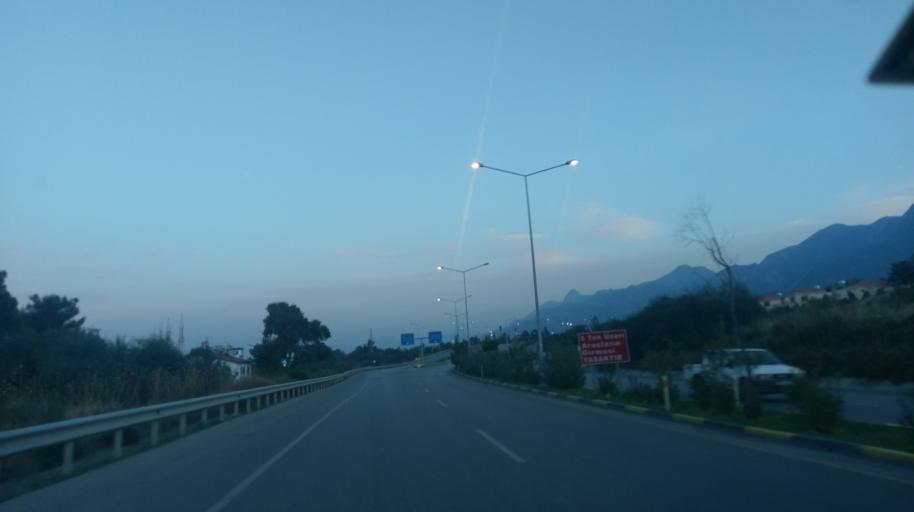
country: CY
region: Keryneia
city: Kyrenia
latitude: 35.3275
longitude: 33.3130
